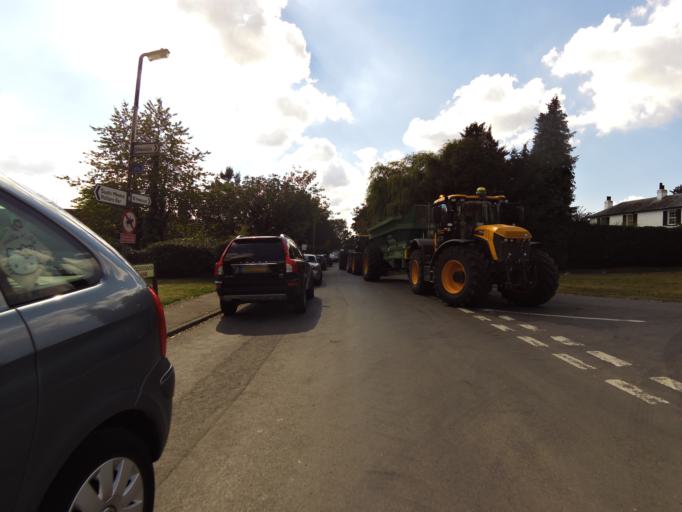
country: GB
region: England
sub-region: Hertfordshire
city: Shenley AV
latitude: 51.6891
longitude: -0.2445
